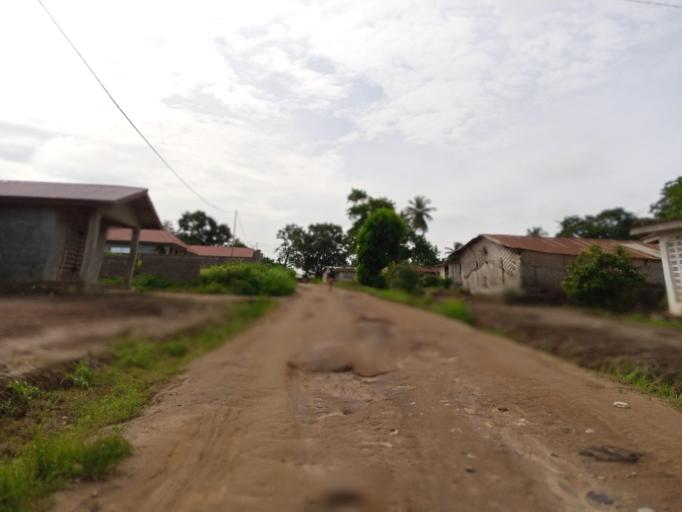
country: SL
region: Northern Province
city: Masoyila
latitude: 8.6078
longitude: -13.1988
